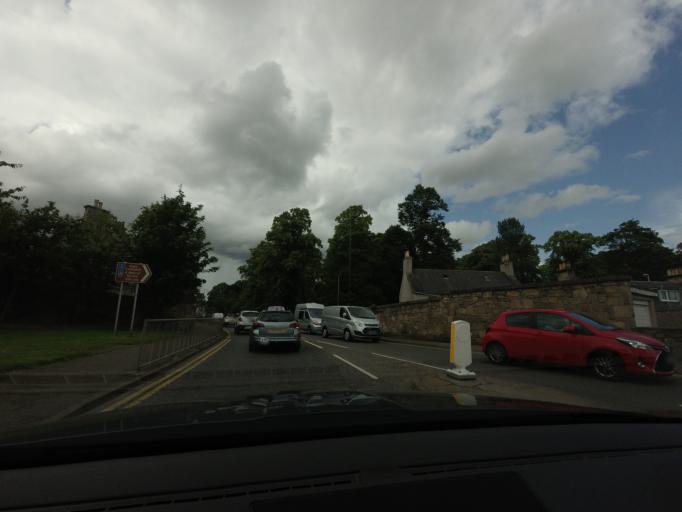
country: GB
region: Scotland
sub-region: Moray
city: Elgin
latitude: 57.6491
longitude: -3.3085
